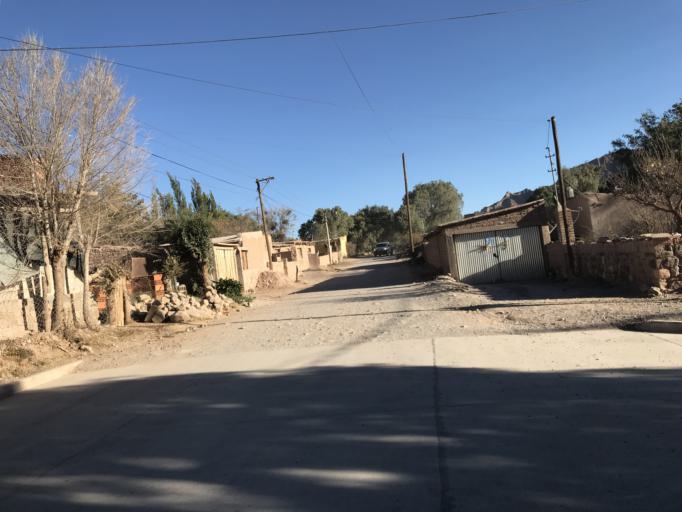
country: AR
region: Jujuy
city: Maimara
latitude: -23.5781
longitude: -65.4012
